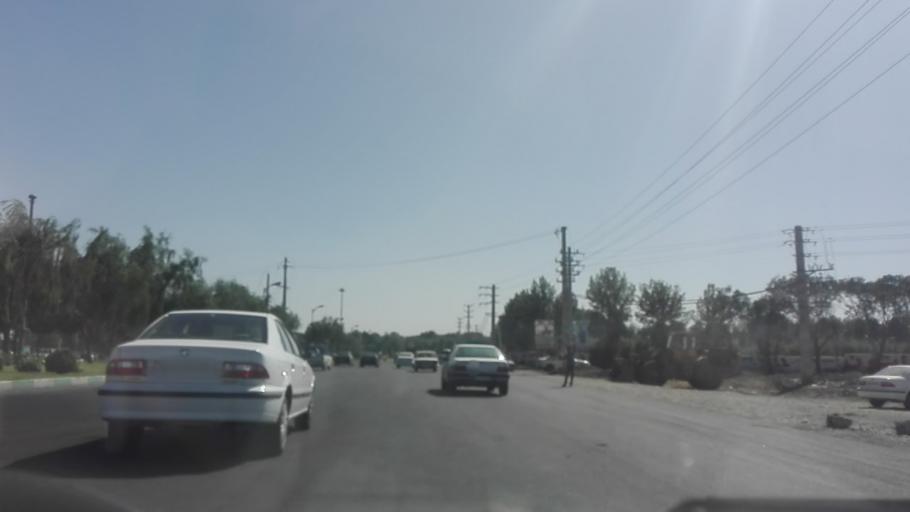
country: IR
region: Tehran
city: Shahre Jadide Andisheh
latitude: 35.6563
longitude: 51.0053
